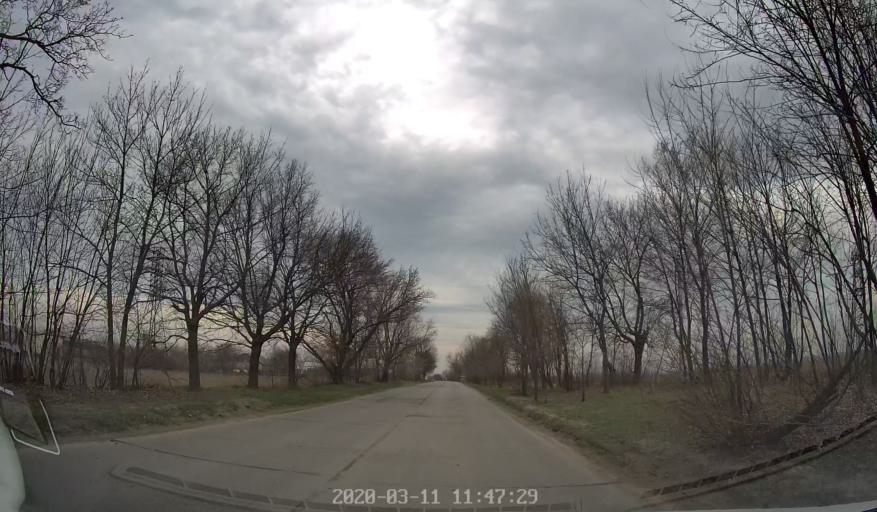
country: MD
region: Chisinau
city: Chisinau
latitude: 46.9548
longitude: 28.8656
